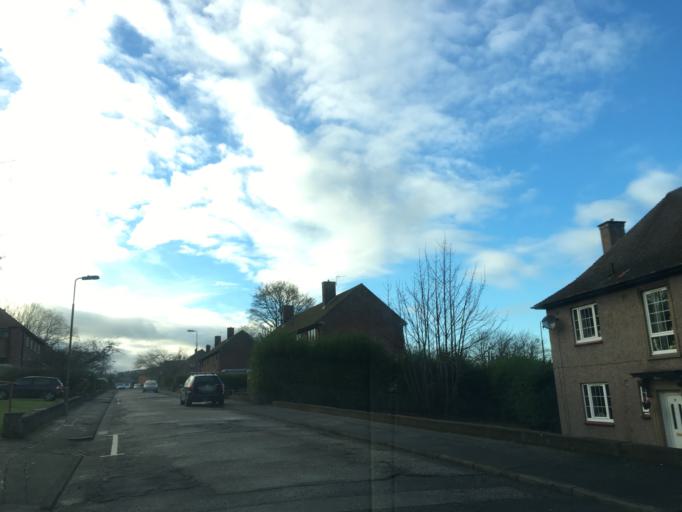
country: GB
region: Scotland
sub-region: Edinburgh
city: Colinton
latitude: 55.9074
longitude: -3.2392
